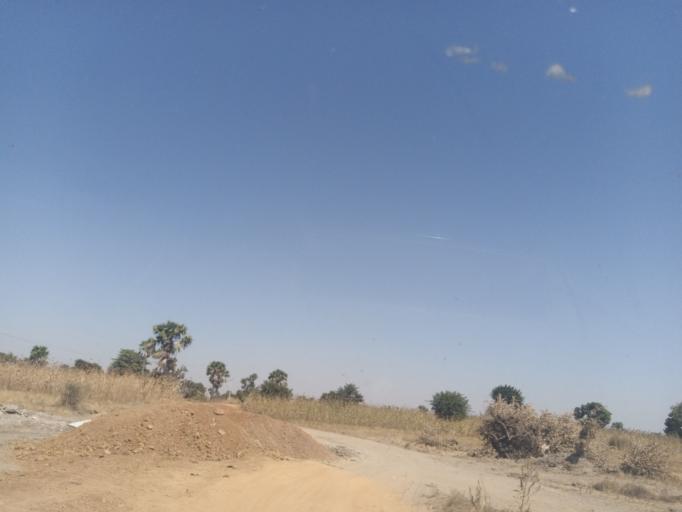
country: NG
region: Adamawa
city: Yola
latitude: 9.2961
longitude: 12.8867
